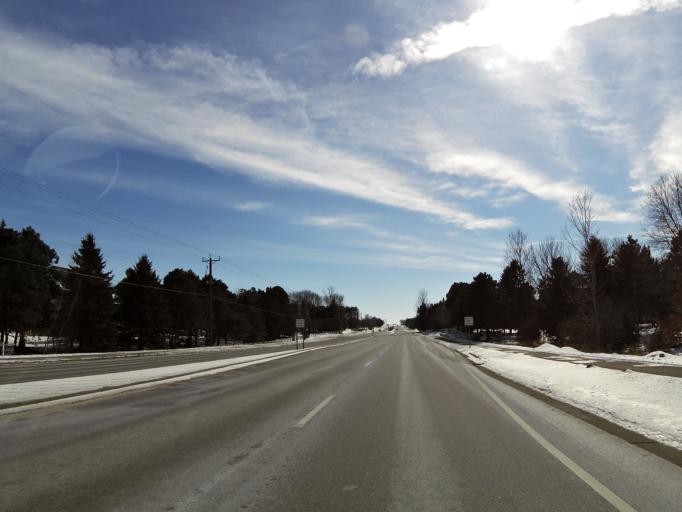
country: US
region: Minnesota
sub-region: Washington County
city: Woodbury
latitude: 44.9004
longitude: -92.9036
